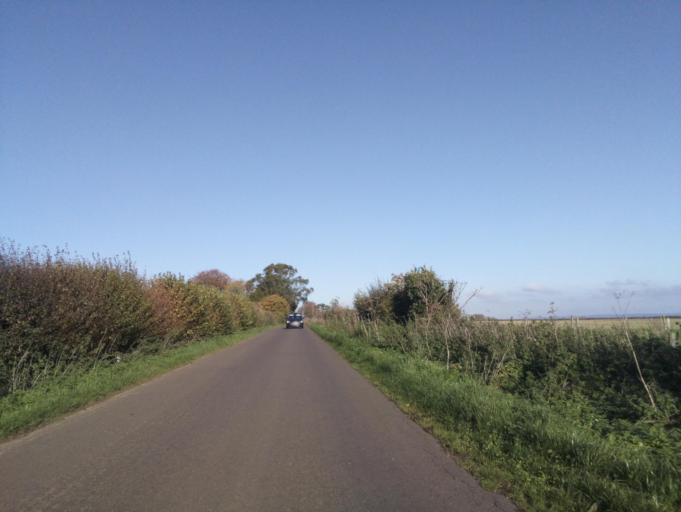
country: GB
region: England
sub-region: Dorset
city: Sherborne
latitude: 51.0083
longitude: -2.5097
